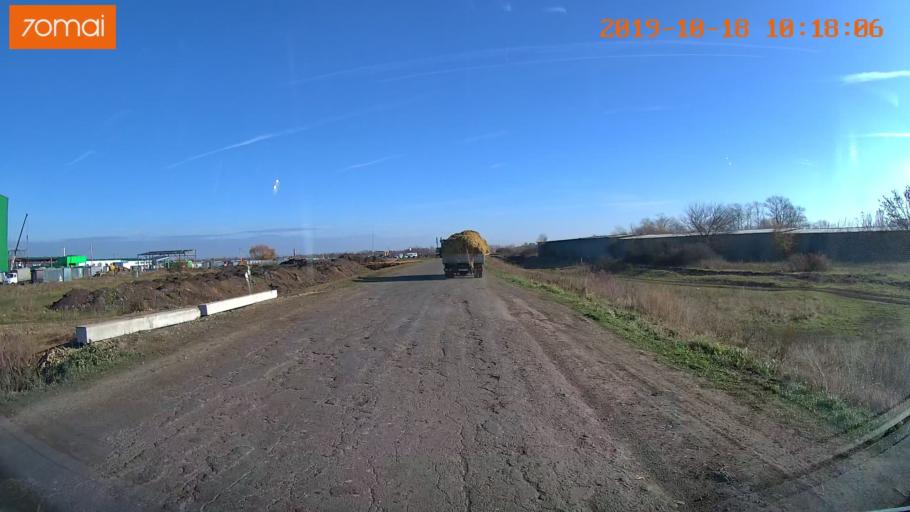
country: RU
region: Tula
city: Kurkino
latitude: 53.4162
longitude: 38.6296
